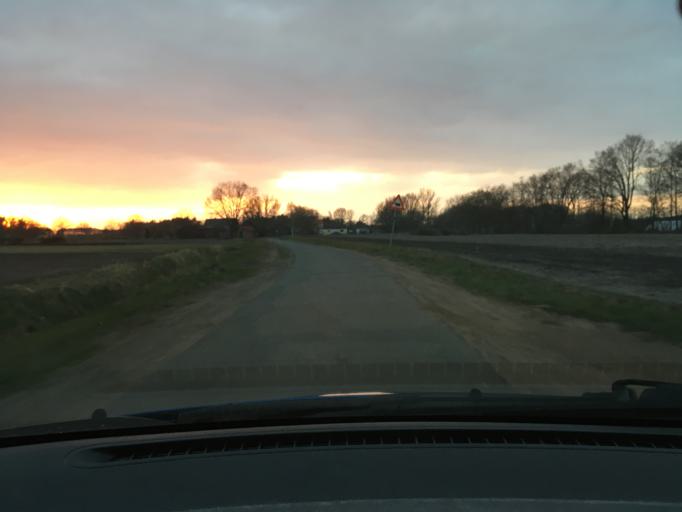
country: DE
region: Lower Saxony
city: Bleckede
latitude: 53.2984
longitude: 10.6768
